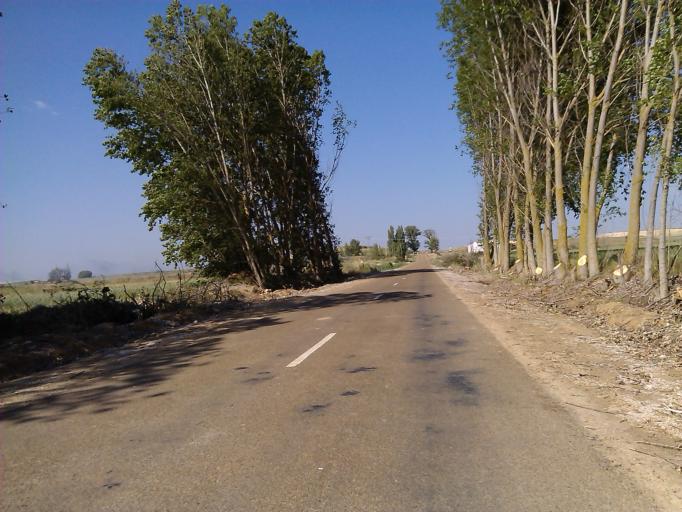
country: ES
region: Castille and Leon
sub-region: Provincia de Palencia
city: Melgar de Yuso
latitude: 42.2678
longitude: -4.2686
